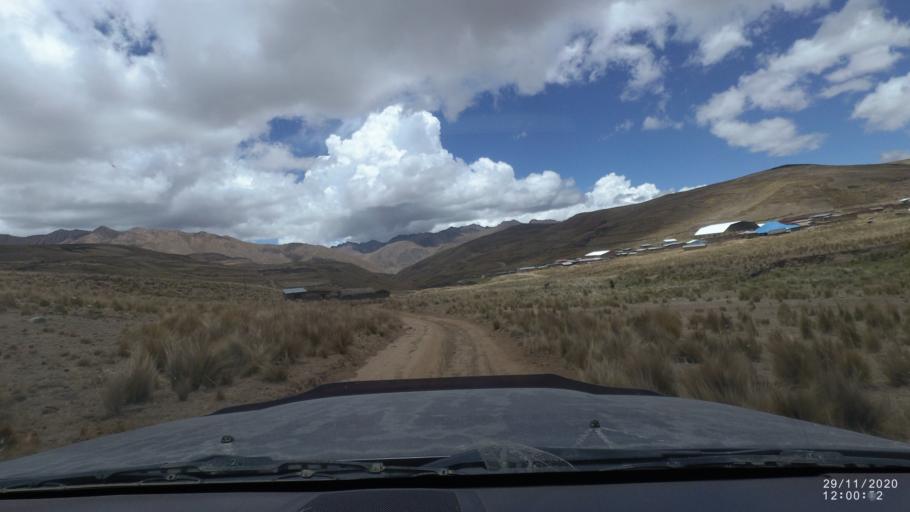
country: BO
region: Cochabamba
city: Cochabamba
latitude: -17.1514
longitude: -66.2794
